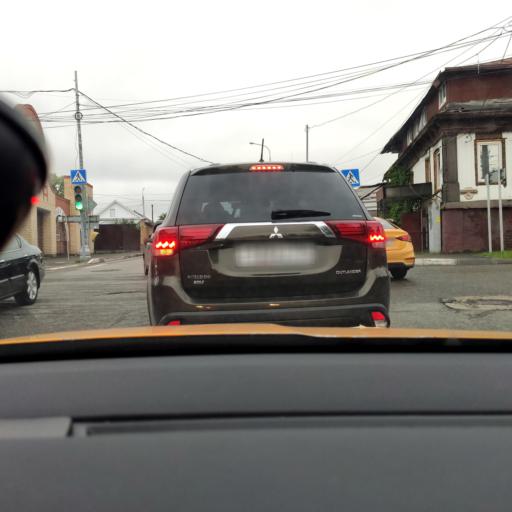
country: RU
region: Moskovskaya
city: Serpukhov
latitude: 54.9094
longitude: 37.4032
